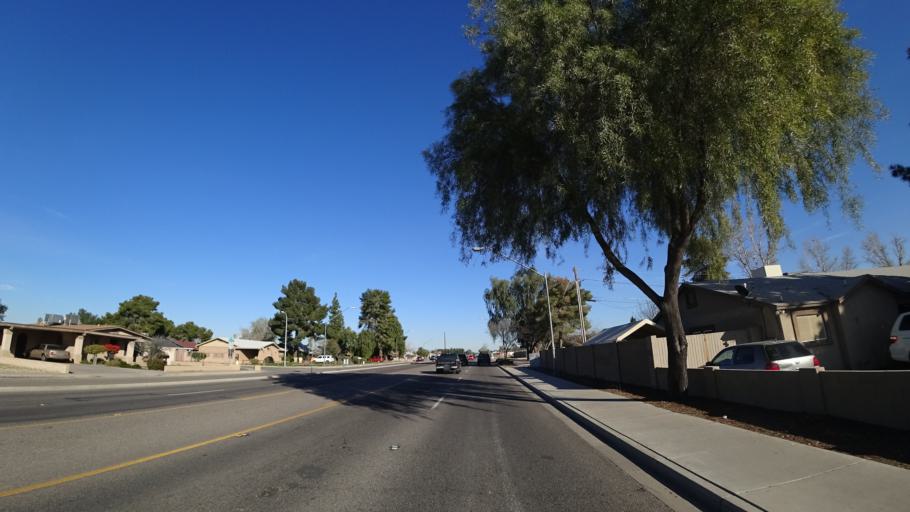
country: US
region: Arizona
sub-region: Maricopa County
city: Glendale
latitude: 33.5235
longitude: -112.2150
